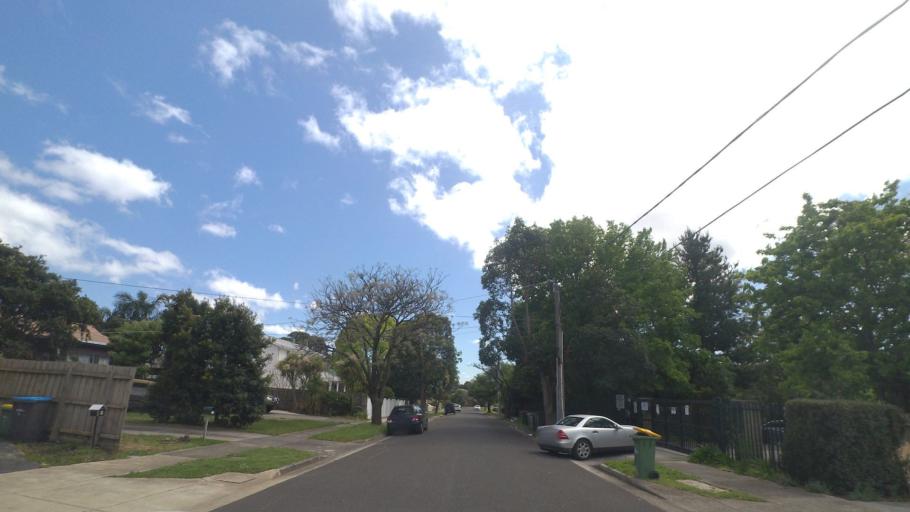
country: AU
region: Victoria
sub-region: Knox
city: Bayswater
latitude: -37.8504
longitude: 145.2734
